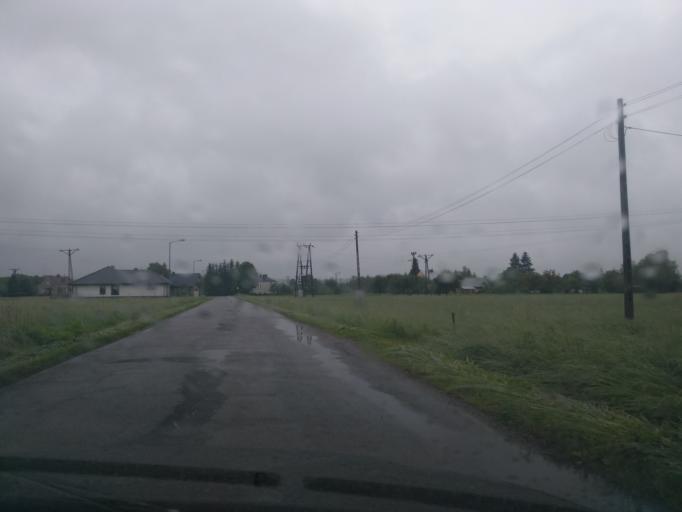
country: PL
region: Subcarpathian Voivodeship
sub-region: Powiat jasielski
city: Jaslo
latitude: 49.7442
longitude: 21.4982
